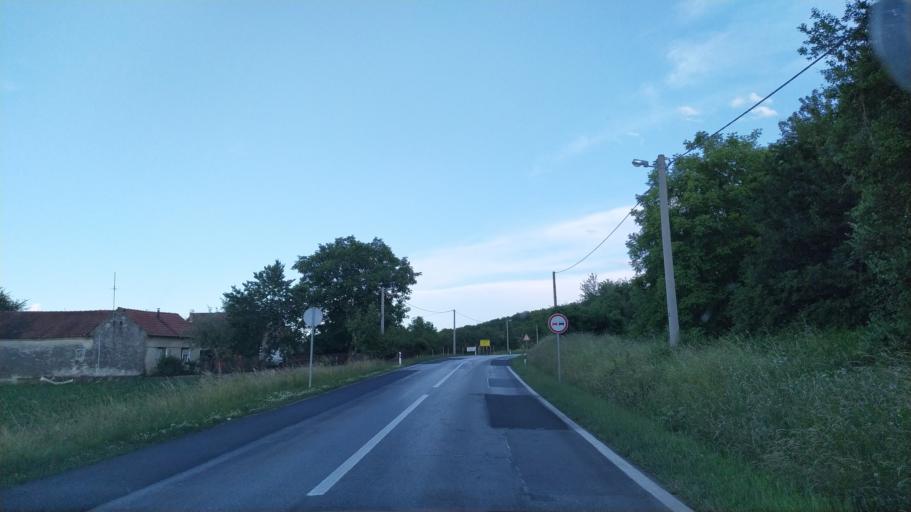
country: HR
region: Virovitick-Podravska
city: Slatina
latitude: 45.7432
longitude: 17.6035
